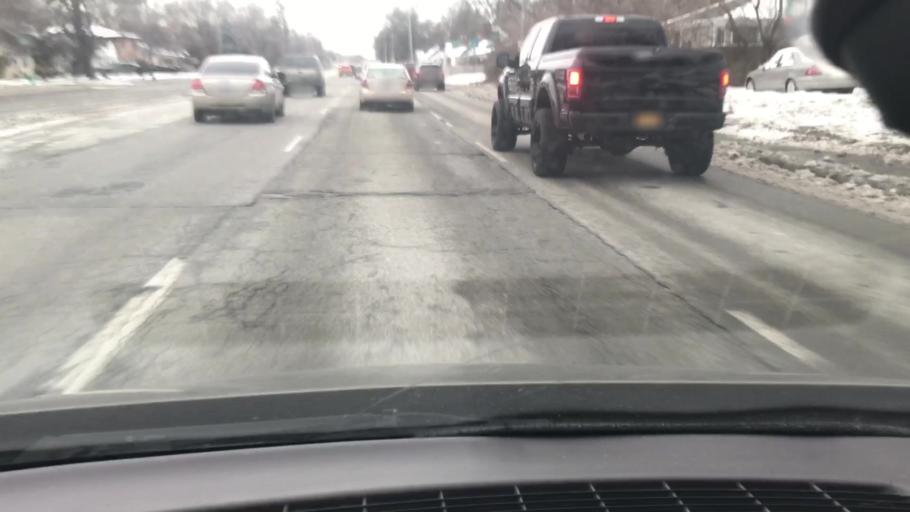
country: US
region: Indiana
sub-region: Marion County
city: Broad Ripple
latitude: 39.8582
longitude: -86.1221
